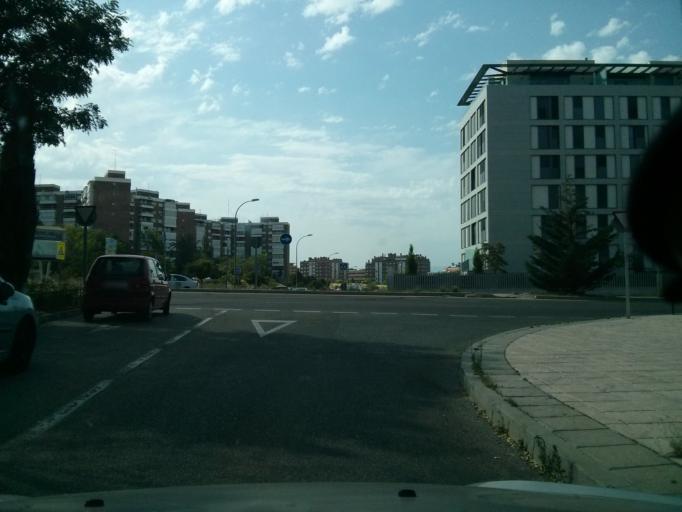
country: ES
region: Madrid
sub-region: Provincia de Madrid
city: Pinar de Chamartin
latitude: 40.4871
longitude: -3.6579
